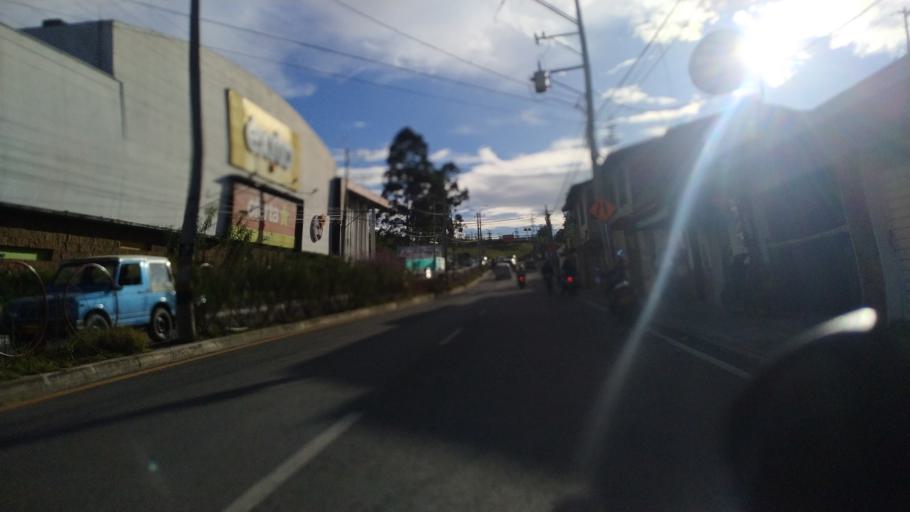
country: CO
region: Antioquia
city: Rionegro
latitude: 6.1490
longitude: -75.3778
